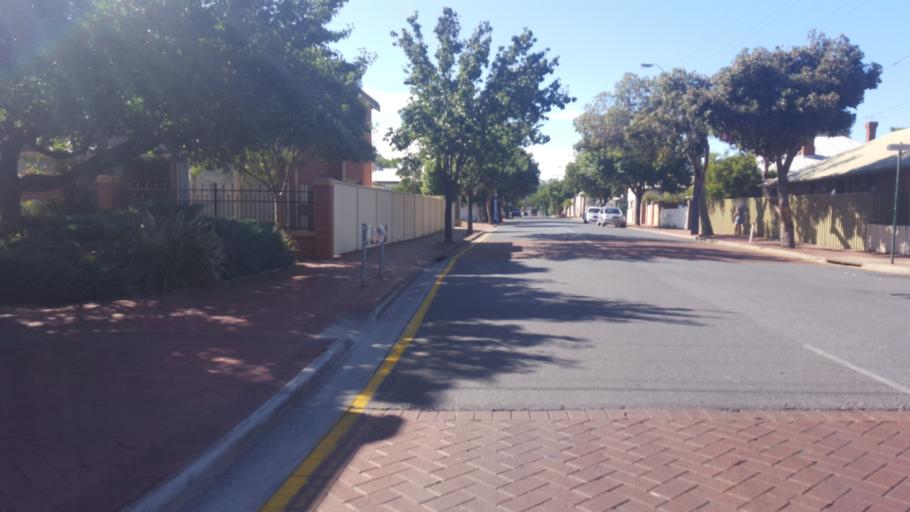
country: AU
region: South Australia
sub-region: Adelaide
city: North Adelaide
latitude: -34.9002
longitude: 138.5804
